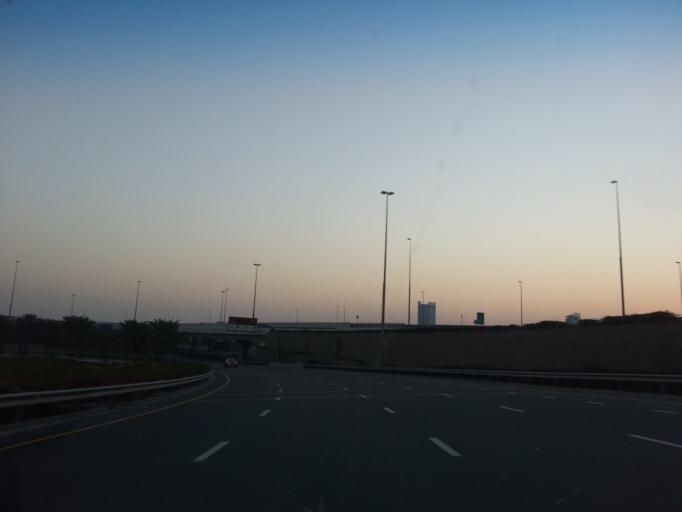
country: AE
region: Dubai
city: Dubai
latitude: 25.0580
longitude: 55.2478
